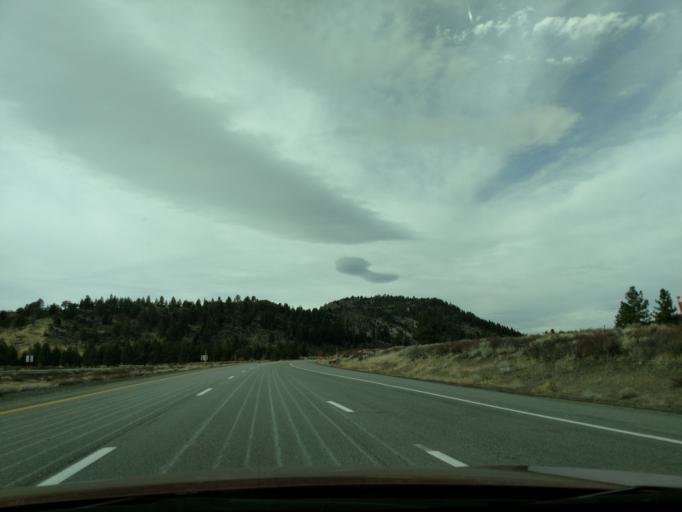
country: US
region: California
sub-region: Mono County
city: Mammoth Lakes
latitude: 37.6434
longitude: -118.9199
